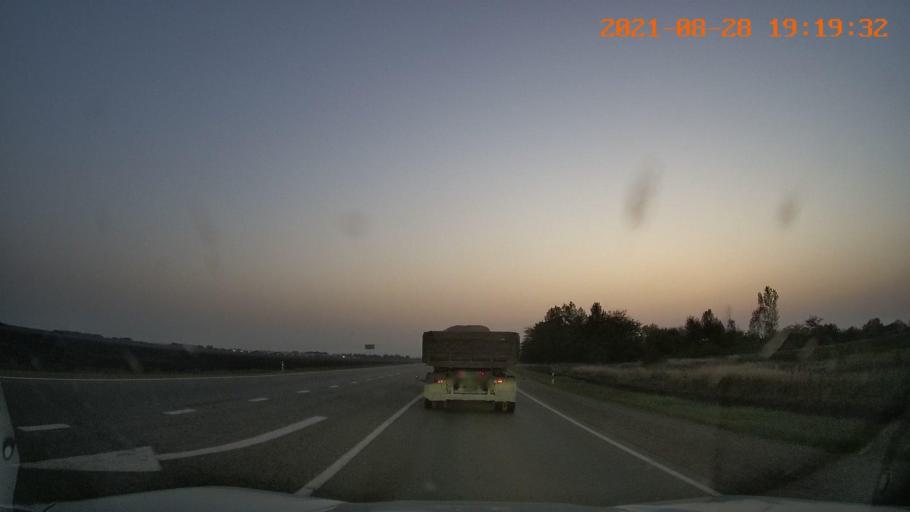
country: RU
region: Krasnodarskiy
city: Ryazanskaya
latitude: 44.8906
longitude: 39.5144
